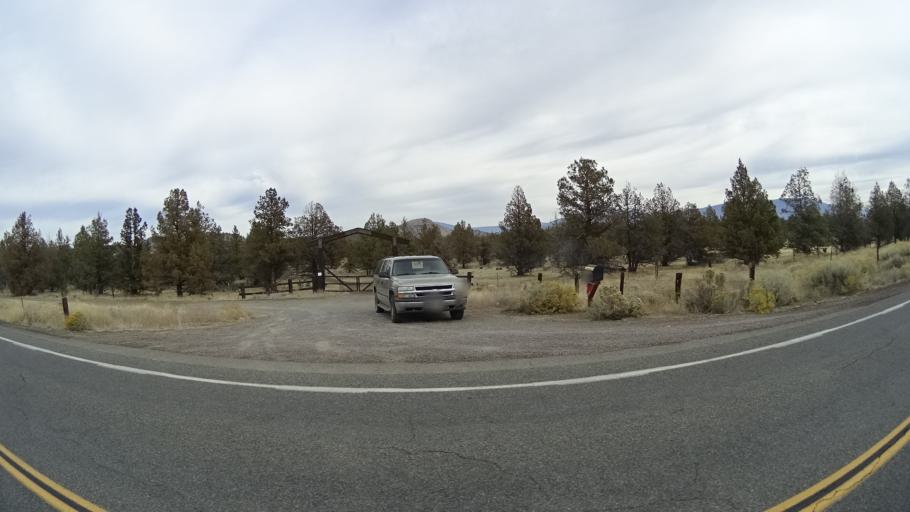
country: US
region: California
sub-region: Siskiyou County
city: Montague
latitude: 41.6375
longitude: -122.4564
